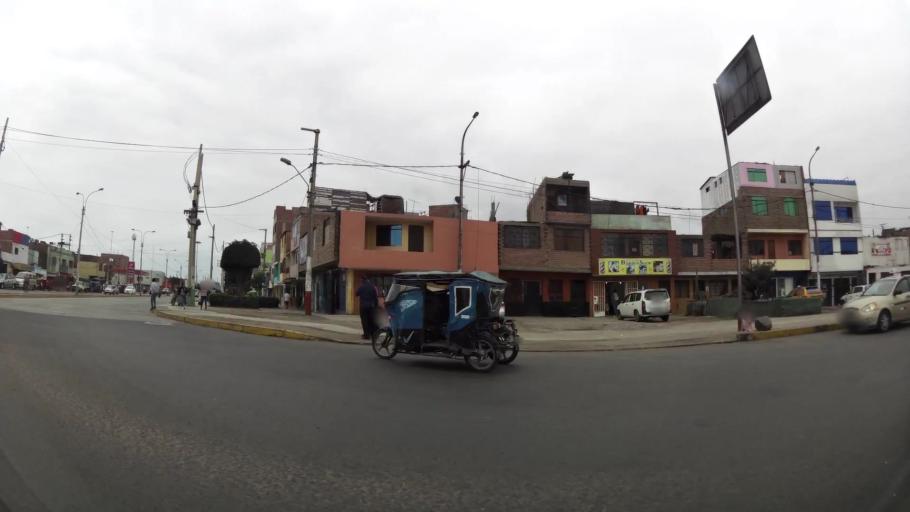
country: PE
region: Callao
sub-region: Callao
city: Callao
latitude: -12.0512
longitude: -77.1340
